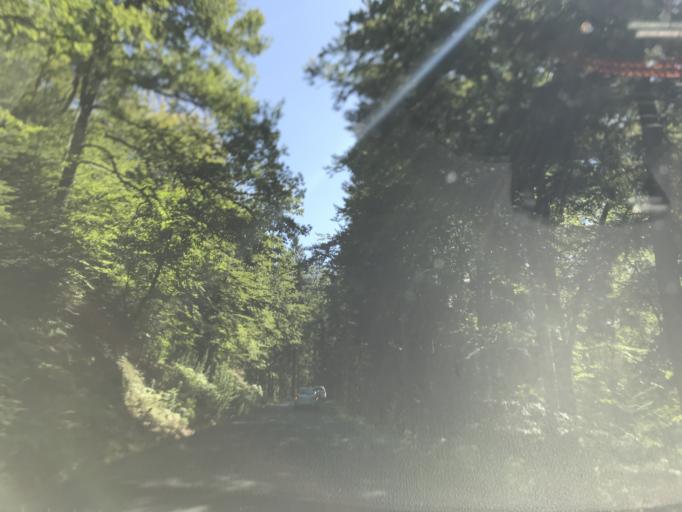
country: FR
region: Auvergne
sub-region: Departement du Puy-de-Dome
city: Job
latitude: 45.6622
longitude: 3.7175
